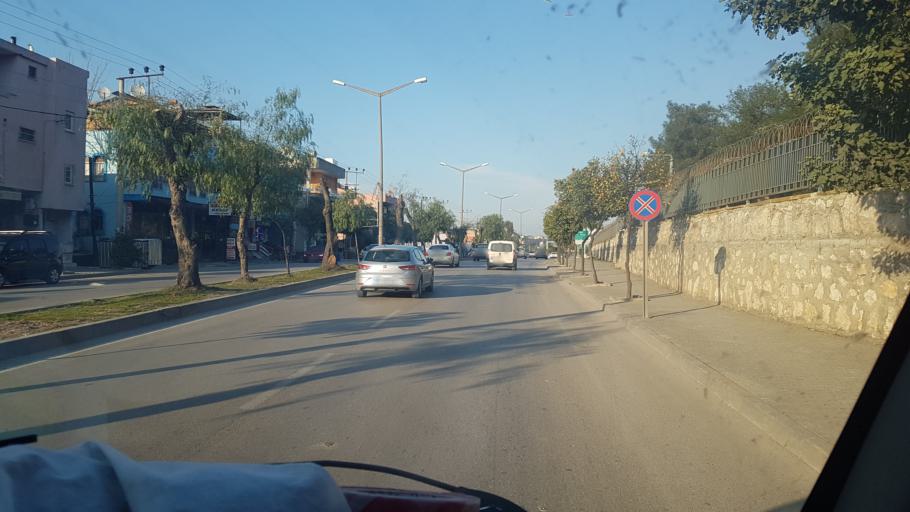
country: TR
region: Adana
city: Adana
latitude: 37.0177
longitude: 35.3406
